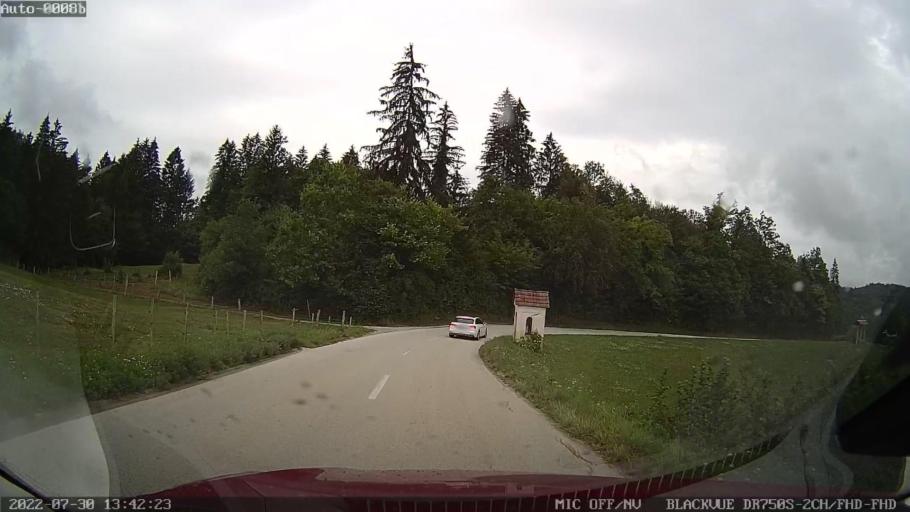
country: SI
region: Ivancna Gorica
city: Sentvid pri Sticni
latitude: 45.9061
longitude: 14.8956
